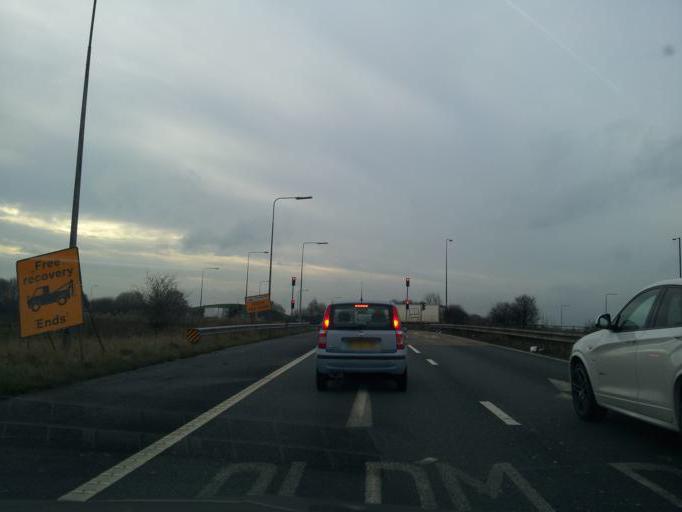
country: GB
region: England
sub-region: Borough of Rochdale
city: Rochdale
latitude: 53.5873
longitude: -2.1550
